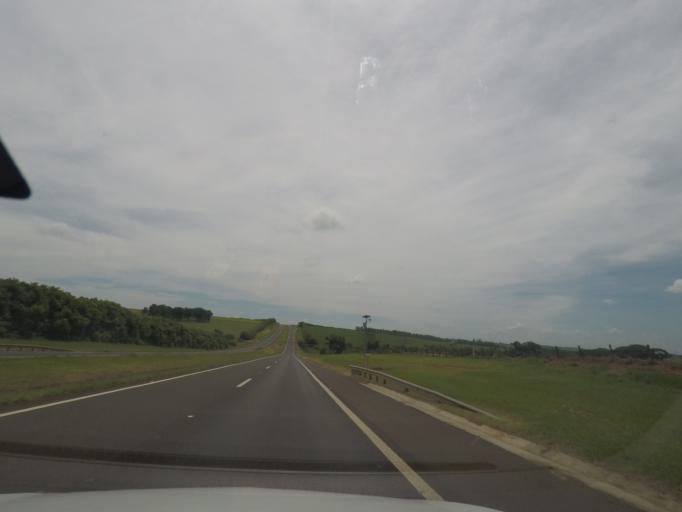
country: BR
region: Sao Paulo
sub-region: Bebedouro
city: Bebedouro
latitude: -21.0184
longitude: -48.4247
